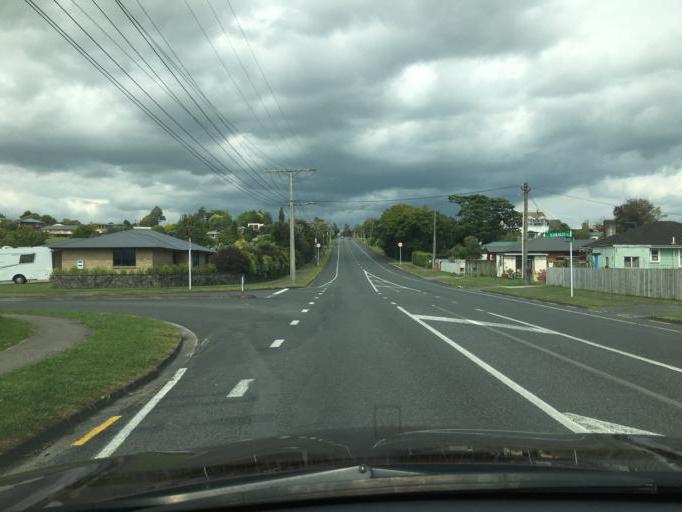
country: NZ
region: Waikato
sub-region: Waipa District
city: Cambridge
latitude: -38.0064
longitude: 175.3430
